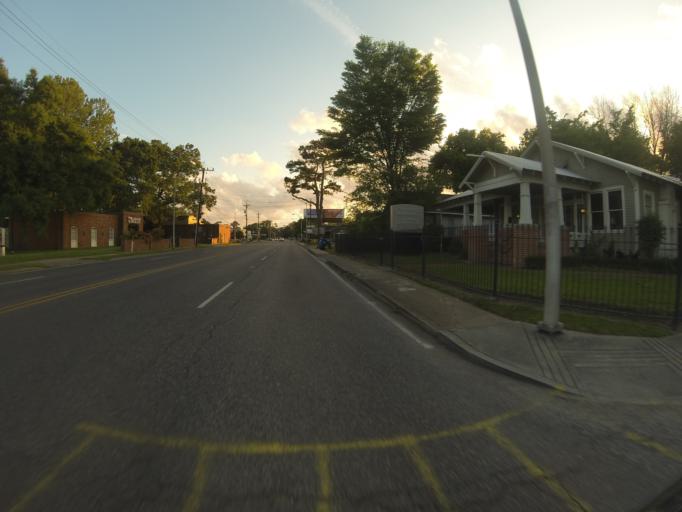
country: US
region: Louisiana
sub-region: Lafayette Parish
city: Lafayette
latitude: 30.2215
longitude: -92.0164
